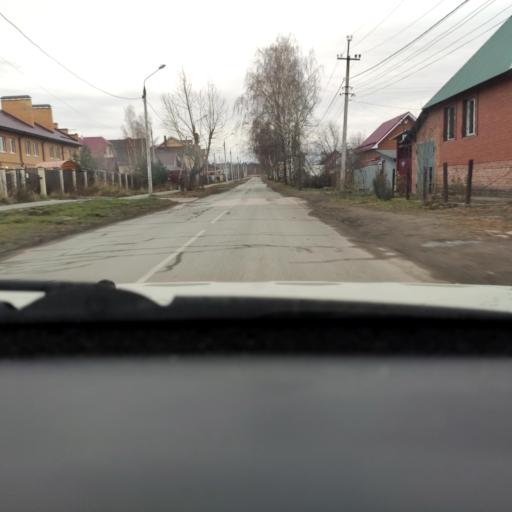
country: RU
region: Perm
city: Polazna
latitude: 58.1275
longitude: 56.3991
